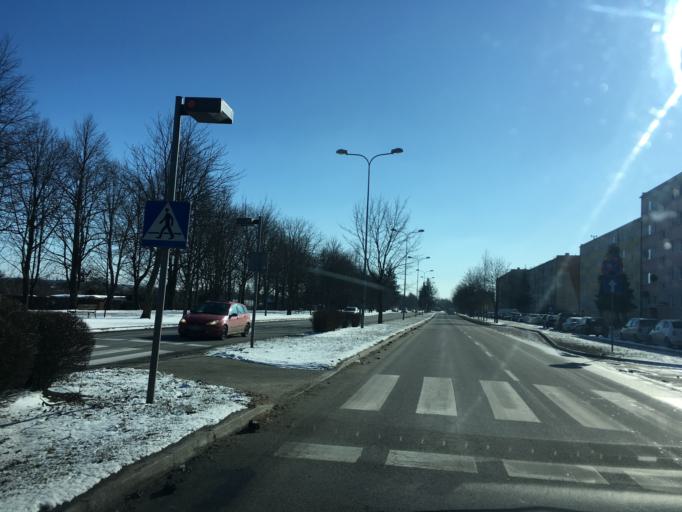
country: PL
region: Pomeranian Voivodeship
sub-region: Slupsk
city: Slupsk
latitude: 54.4722
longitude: 17.0129
